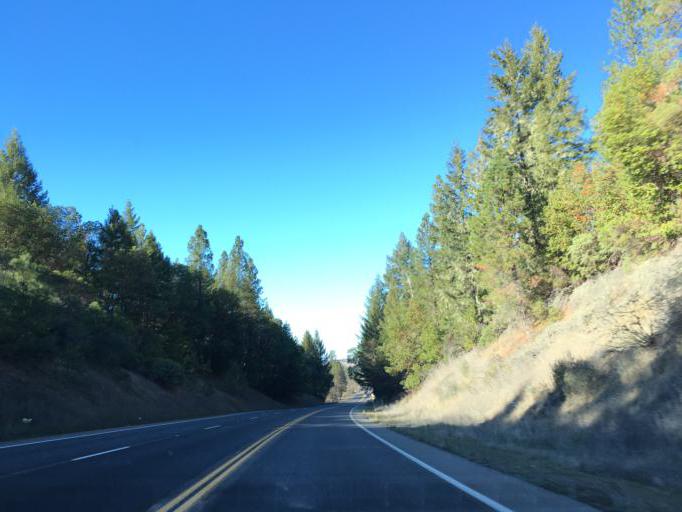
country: US
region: California
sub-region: Mendocino County
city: Laytonville
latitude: 39.7163
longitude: -123.4993
